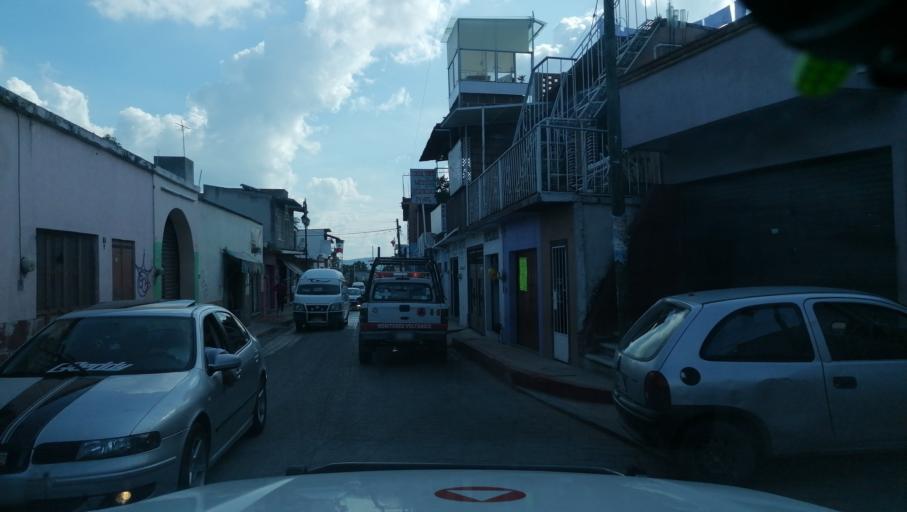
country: MX
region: Morelos
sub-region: Ayala
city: Ciudad Ayala
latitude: 18.7663
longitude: -98.9829
